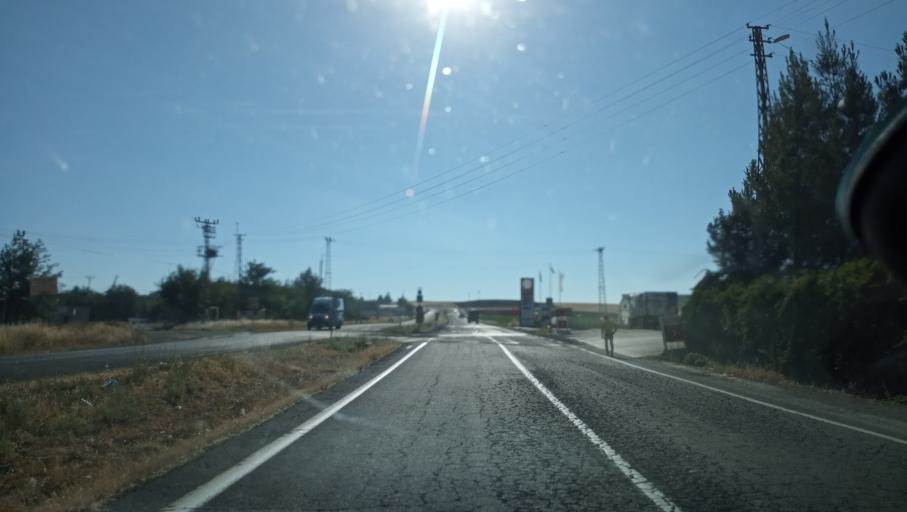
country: TR
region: Diyarbakir
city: Sur
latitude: 37.9910
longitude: 40.3858
